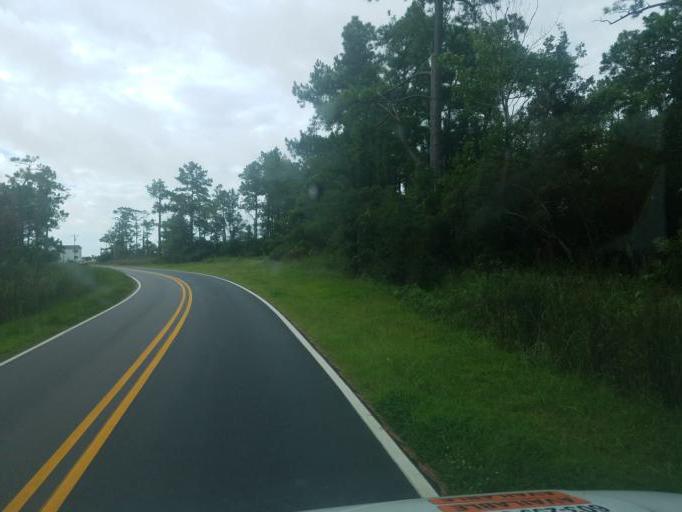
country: US
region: North Carolina
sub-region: Dare County
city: Manteo
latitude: 35.8791
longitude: -75.7590
